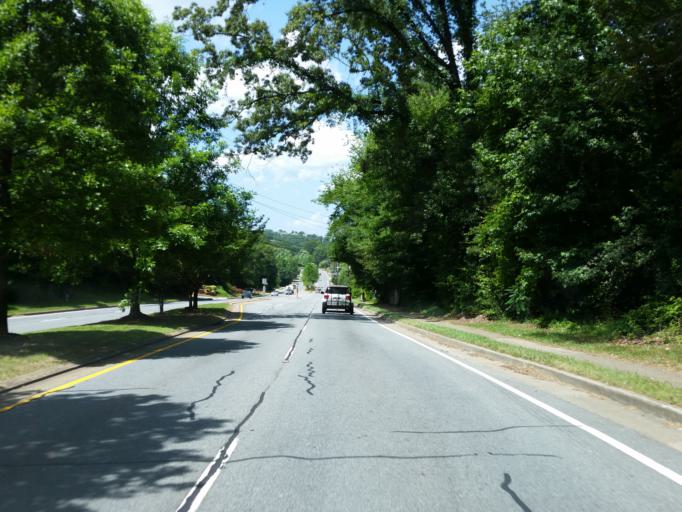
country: US
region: Georgia
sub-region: Cherokee County
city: Woodstock
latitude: 34.0402
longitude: -84.4589
